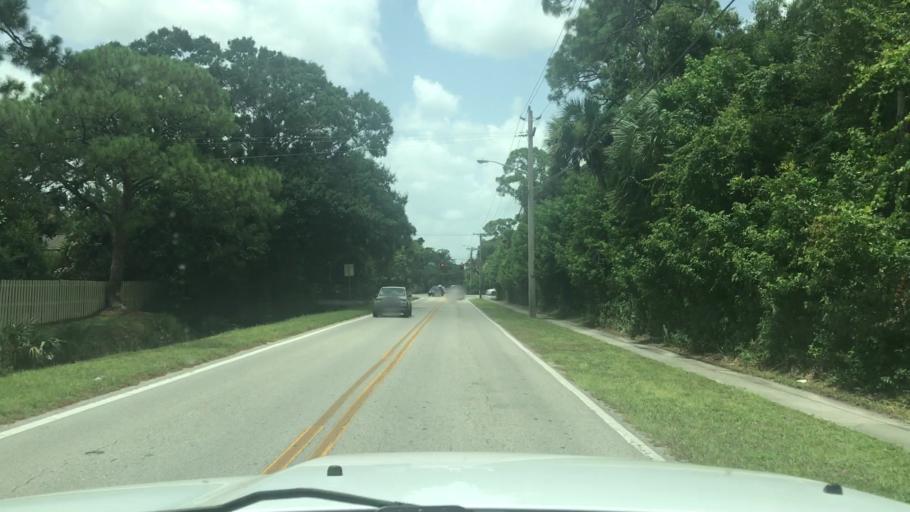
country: US
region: Florida
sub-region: Indian River County
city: Vero Beach South
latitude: 27.6312
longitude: -80.4287
